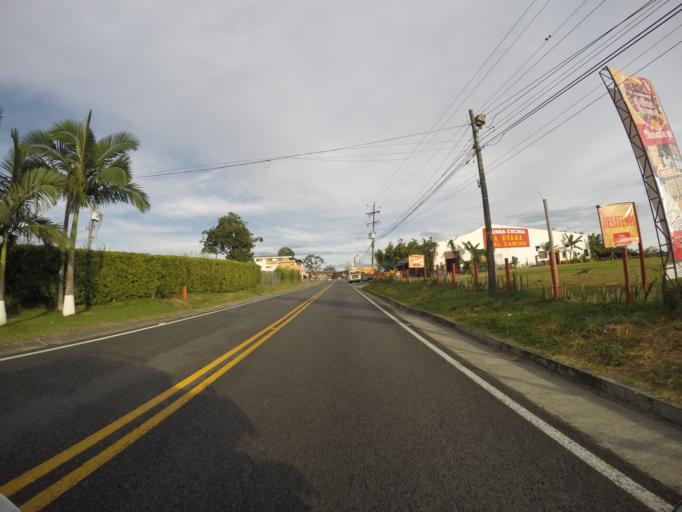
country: CO
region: Risaralda
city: Pereira
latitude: 4.7803
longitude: -75.6969
